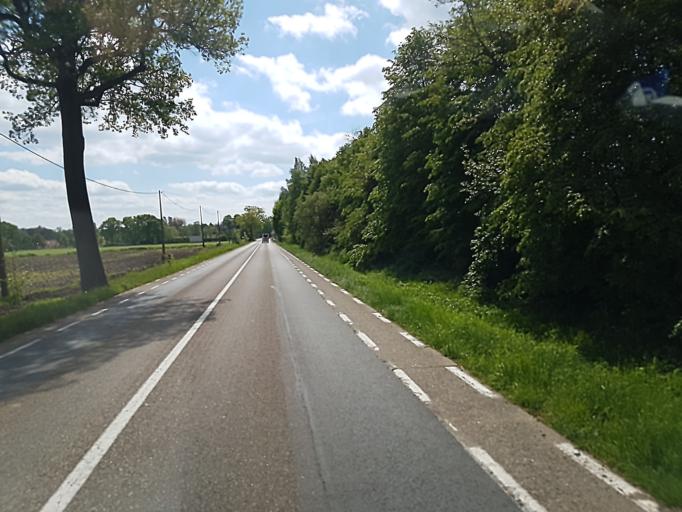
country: BE
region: Flanders
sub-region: Provincie Antwerpen
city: Laakdal
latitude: 51.0624
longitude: 4.9929
